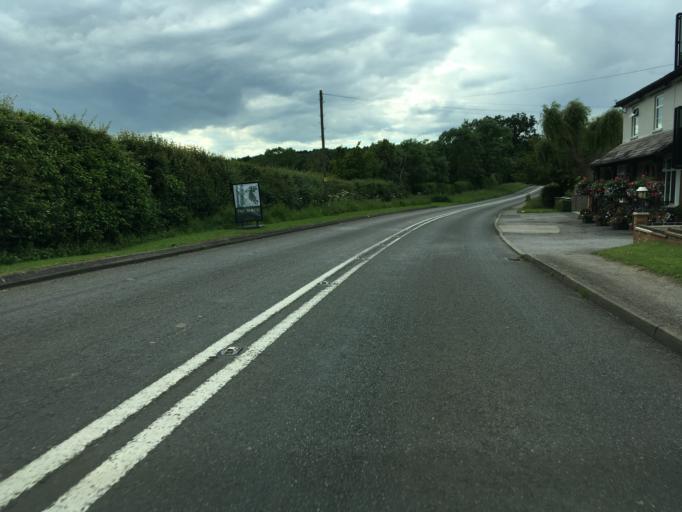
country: GB
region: England
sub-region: Central Bedfordshire
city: Woburn
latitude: 51.9935
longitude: -0.6264
